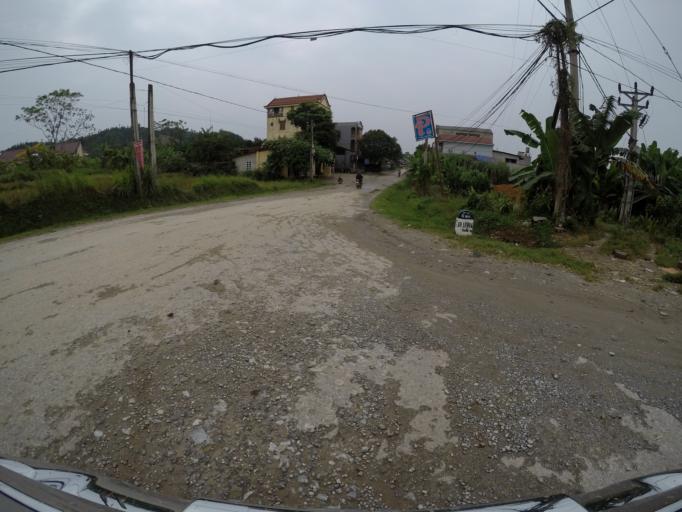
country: VN
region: Yen Bai
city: Co Phuc
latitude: 21.8798
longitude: 104.6744
